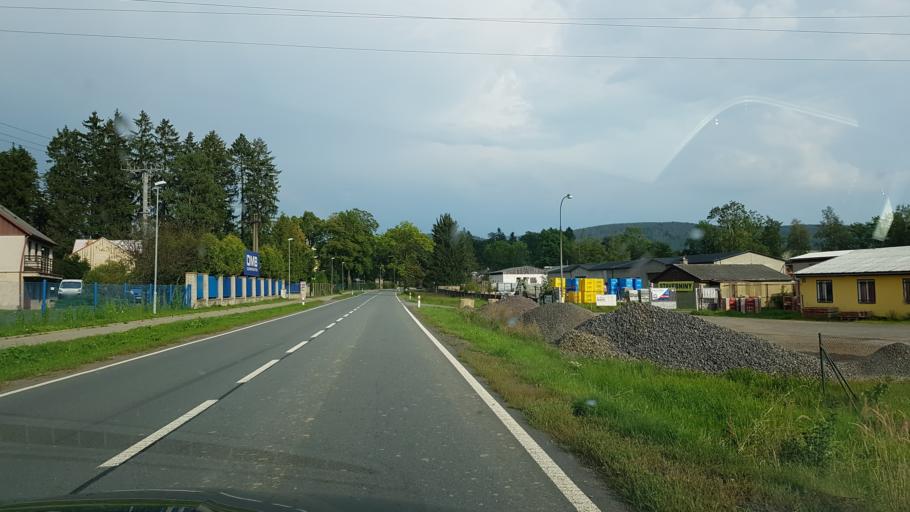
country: CZ
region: Pardubicky
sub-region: Okres Usti nad Orlici
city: Kraliky
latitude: 50.0843
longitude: 16.7447
